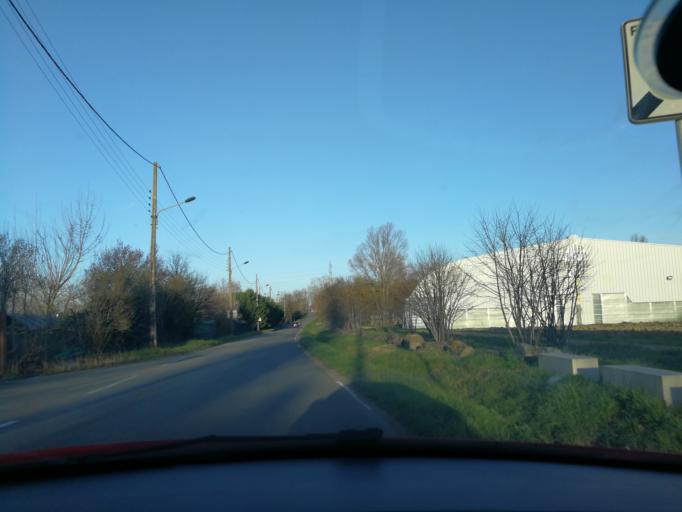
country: FR
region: Midi-Pyrenees
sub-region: Departement de la Haute-Garonne
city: Aucamville
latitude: 43.6560
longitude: 1.4160
